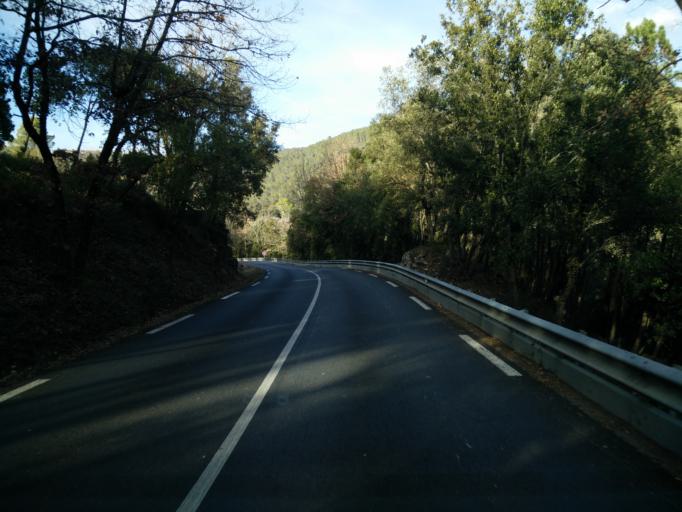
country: FR
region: Provence-Alpes-Cote d'Azur
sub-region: Departement des Alpes-Maritimes
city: Le Tignet
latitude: 43.6211
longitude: 6.8242
